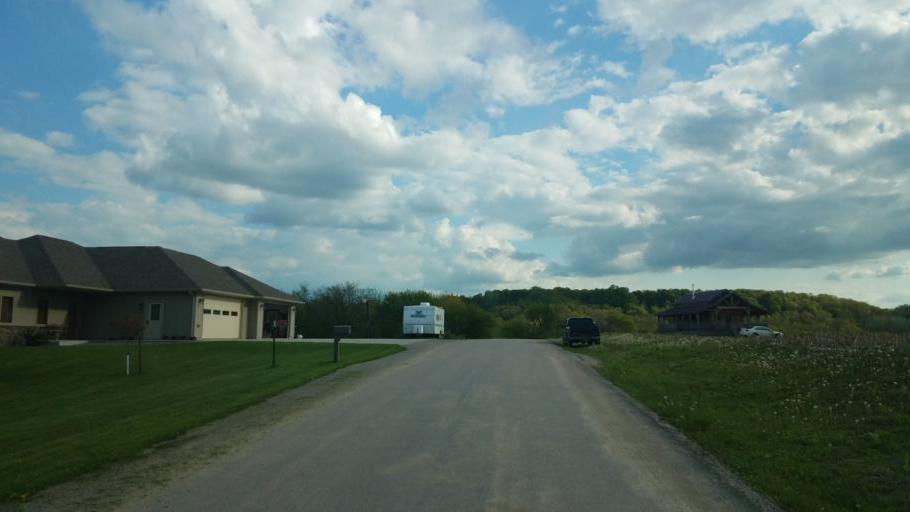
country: US
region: Wisconsin
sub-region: Vernon County
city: Hillsboro
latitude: 43.6534
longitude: -90.3730
